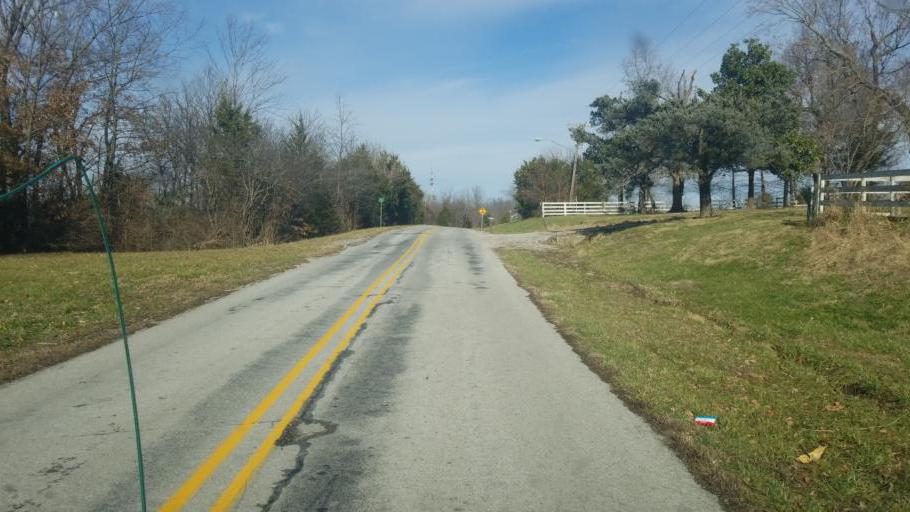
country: US
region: Illinois
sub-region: Jackson County
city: Carbondale
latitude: 37.6978
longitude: -89.2121
